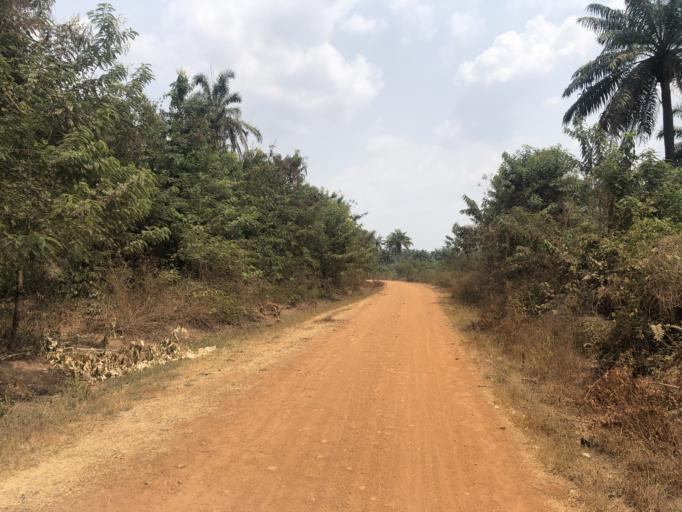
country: NG
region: Osun
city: Bode Osi
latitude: 7.7566
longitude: 4.2491
